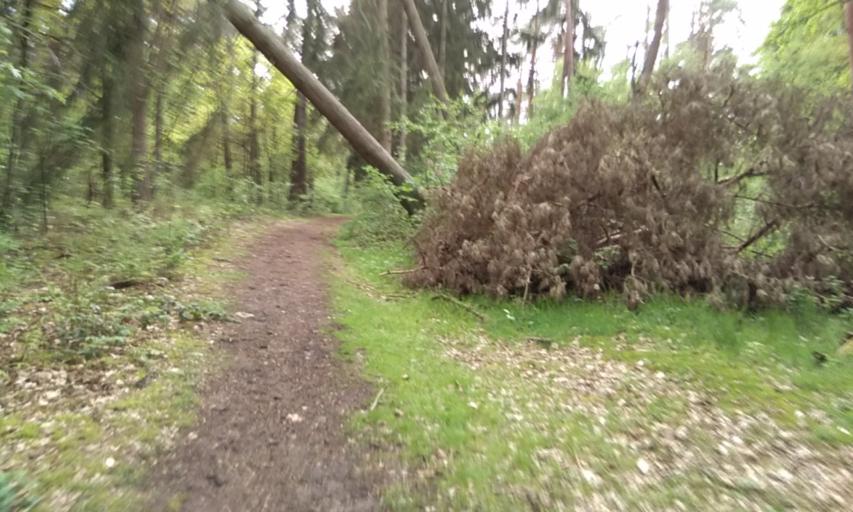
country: DE
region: Lower Saxony
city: Buxtehude
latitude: 53.4508
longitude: 9.6809
